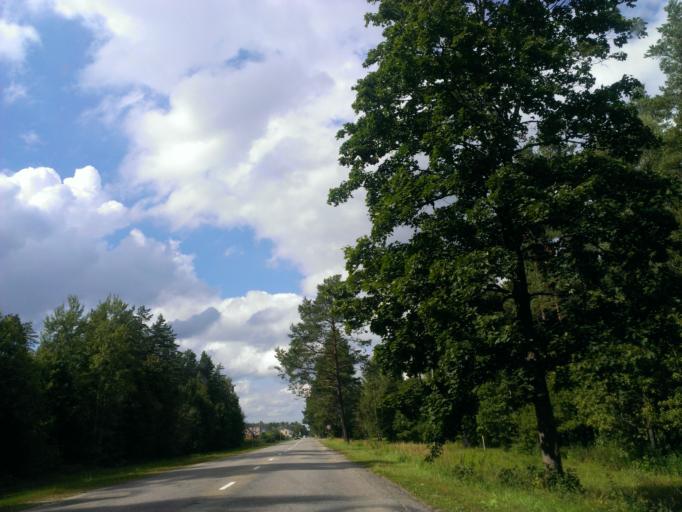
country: LV
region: Garkalne
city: Garkalne
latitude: 56.9670
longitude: 24.4880
